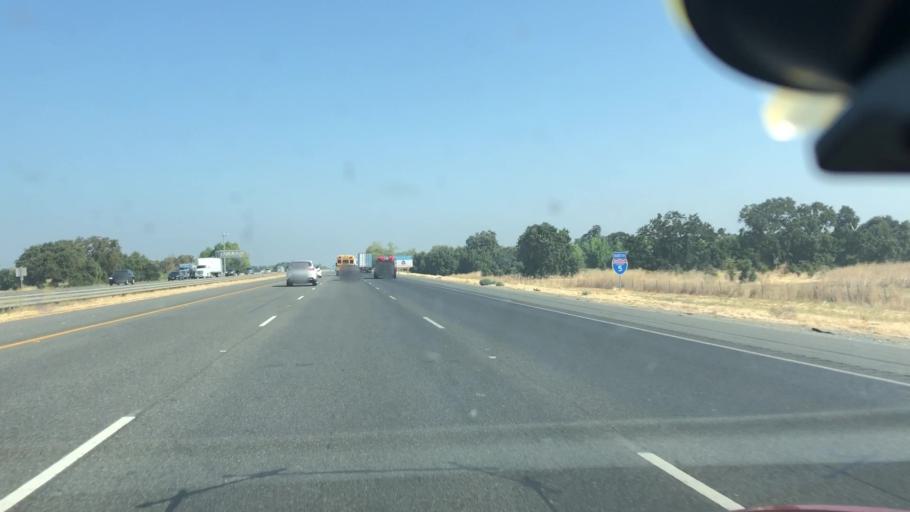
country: US
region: California
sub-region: Sacramento County
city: Laguna
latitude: 38.4361
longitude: -121.4893
